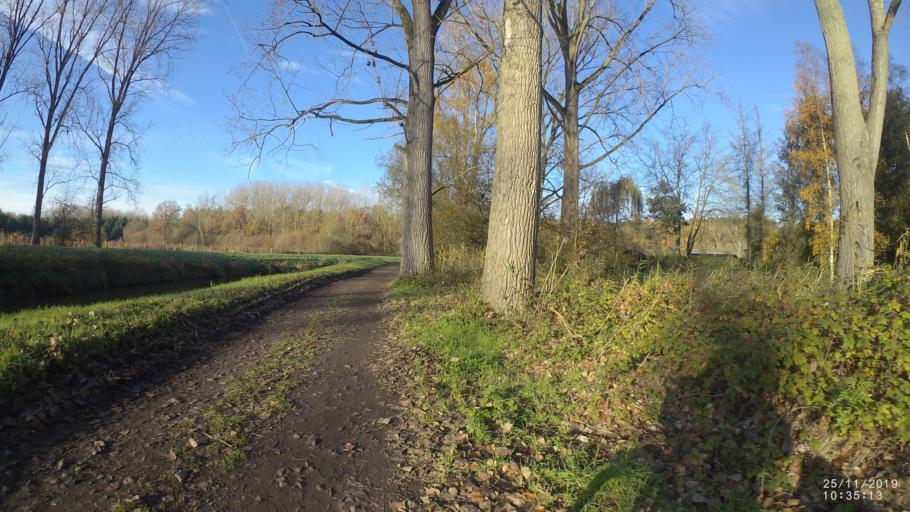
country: BE
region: Flanders
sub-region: Provincie Vlaams-Brabant
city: Scherpenheuvel-Zichem
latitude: 51.0076
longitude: 4.9656
